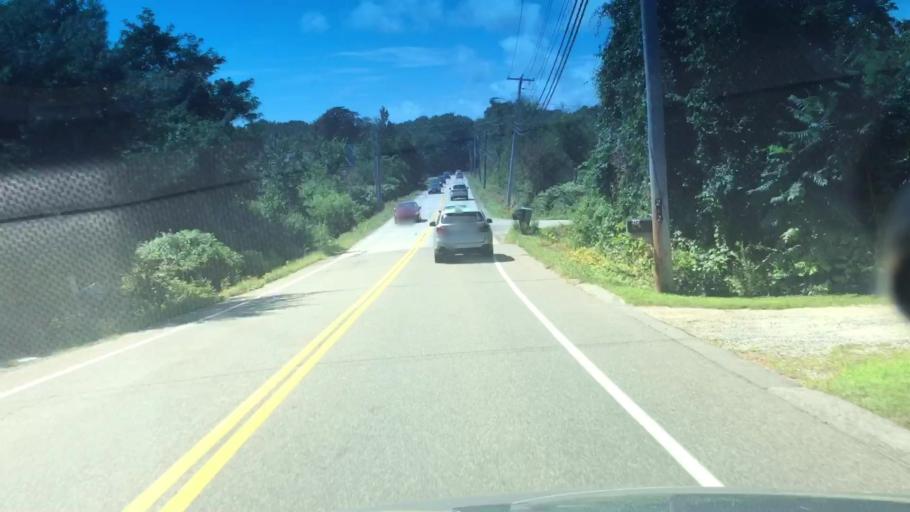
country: US
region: Maine
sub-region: York County
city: York Beach
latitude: 43.1614
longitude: -70.6282
